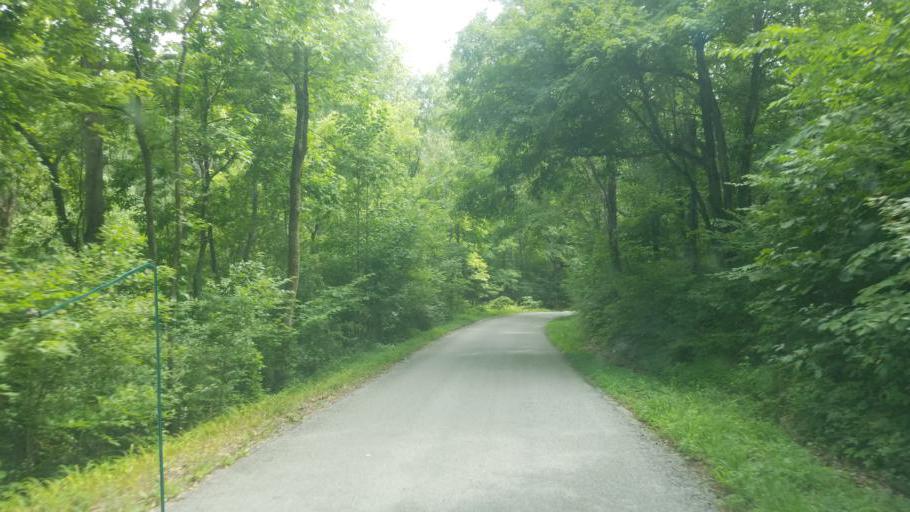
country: US
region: Illinois
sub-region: Union County
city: Cobden
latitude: 37.6205
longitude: -89.3691
